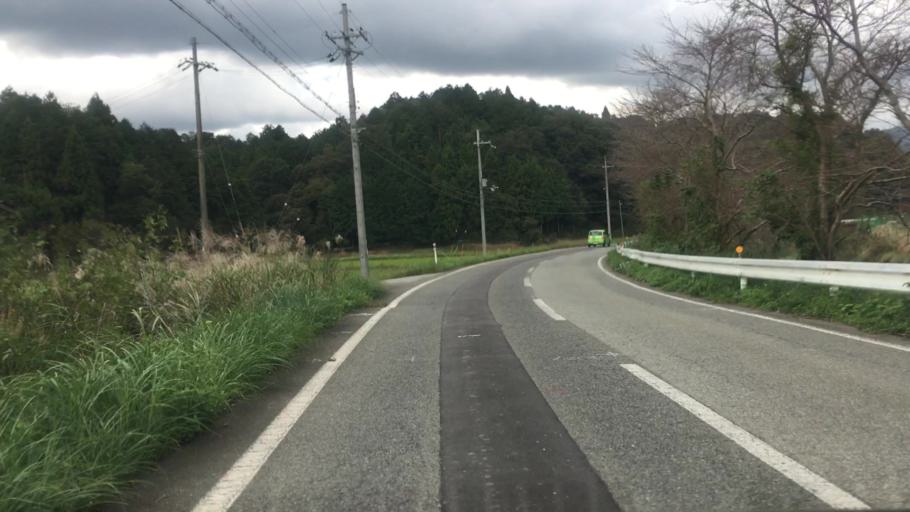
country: JP
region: Hyogo
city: Toyooka
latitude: 35.4430
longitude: 134.7308
